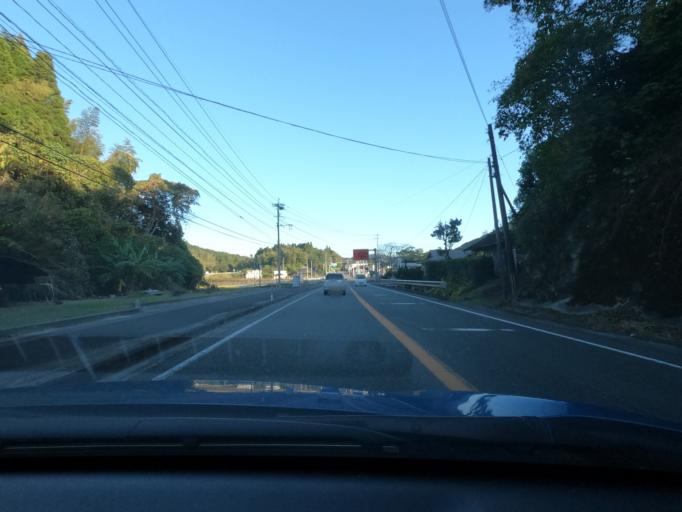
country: JP
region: Kagoshima
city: Satsumasendai
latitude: 31.8485
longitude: 130.2479
